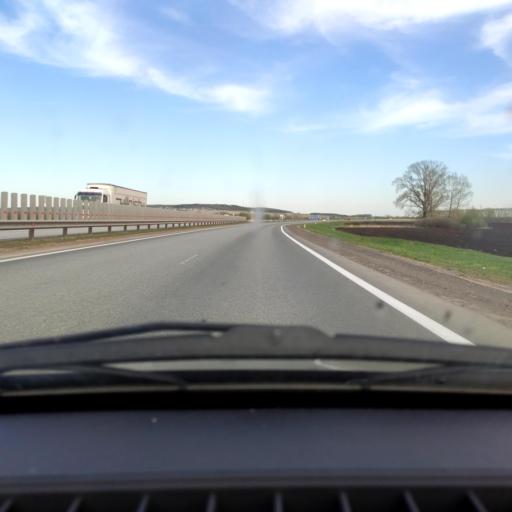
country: RU
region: Bashkortostan
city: Asanovo
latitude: 54.9813
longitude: 55.5570
